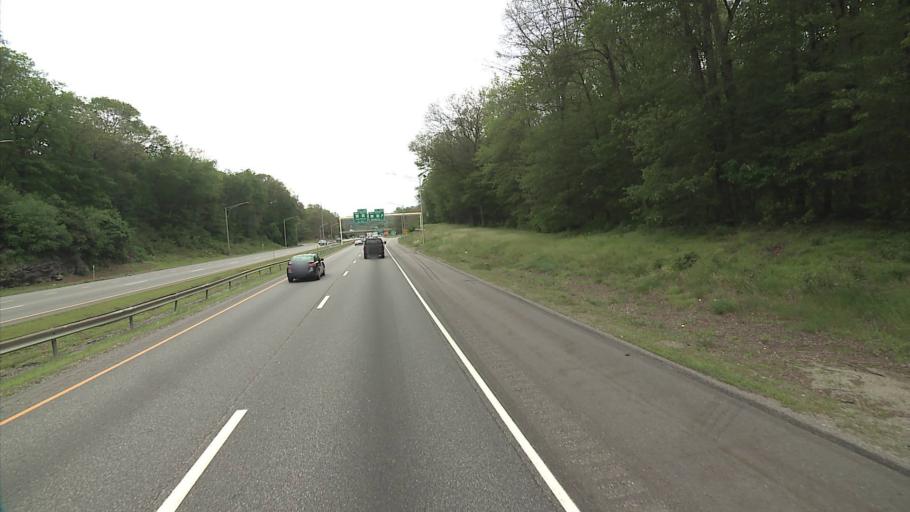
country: US
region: Connecticut
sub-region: New London County
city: Norwich
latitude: 41.5423
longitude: -72.1106
